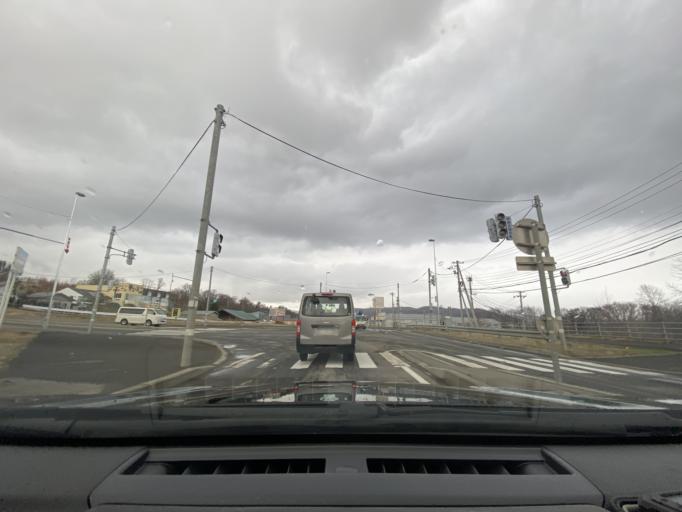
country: JP
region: Hokkaido
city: Otofuke
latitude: 43.2318
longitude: 143.5460
